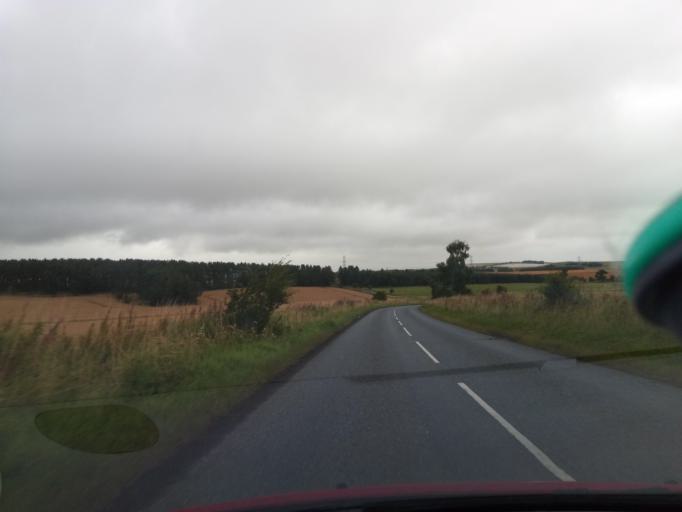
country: GB
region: Scotland
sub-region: The Scottish Borders
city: Earlston
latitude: 55.6592
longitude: -2.5529
